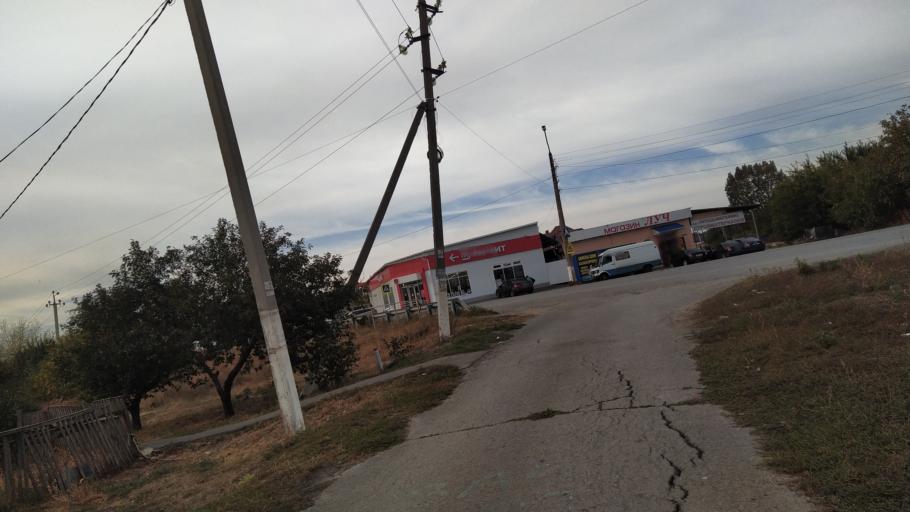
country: RU
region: Rostov
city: Bataysk
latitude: 47.1138
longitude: 39.6774
